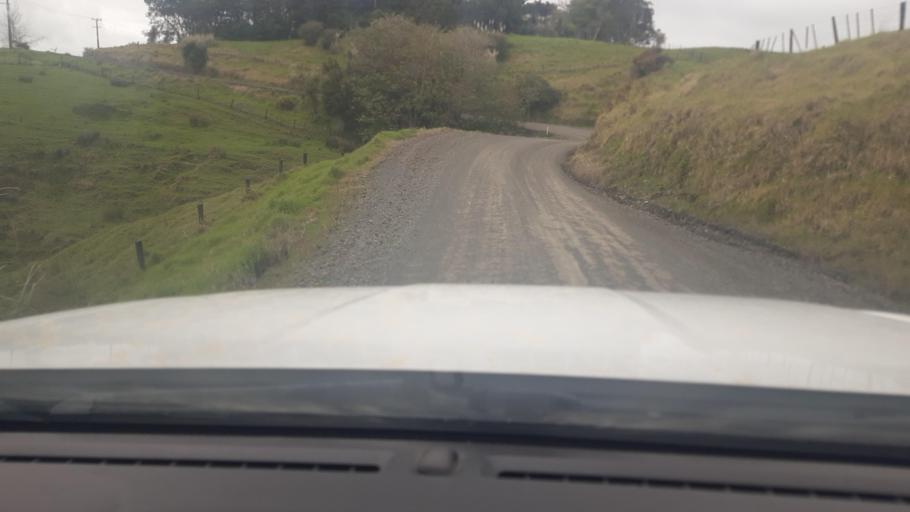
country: NZ
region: Northland
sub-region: Far North District
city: Kaitaia
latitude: -35.0887
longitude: 173.3192
